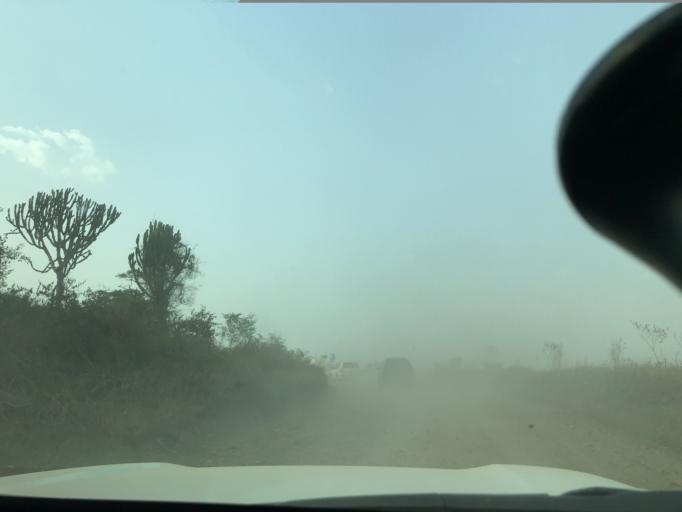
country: CD
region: Nord Kivu
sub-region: North Kivu
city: Butembo
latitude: 0.1417
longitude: 29.6439
